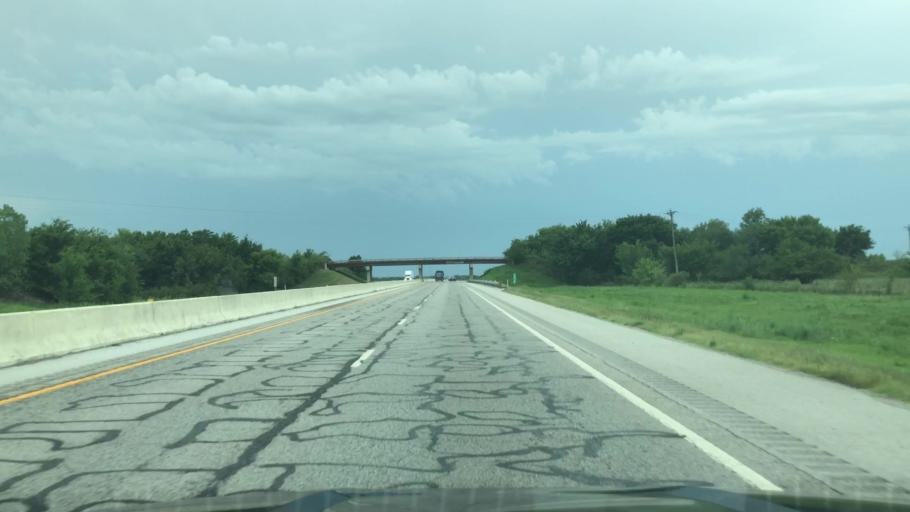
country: US
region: Oklahoma
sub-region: Craig County
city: Vinita
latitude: 36.5255
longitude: -95.2535
